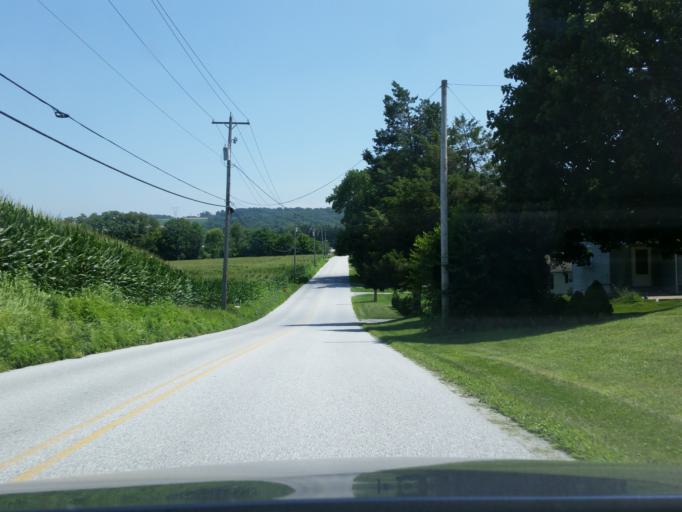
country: US
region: Pennsylvania
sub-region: York County
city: Stonybrook
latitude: 39.9936
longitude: -76.6290
